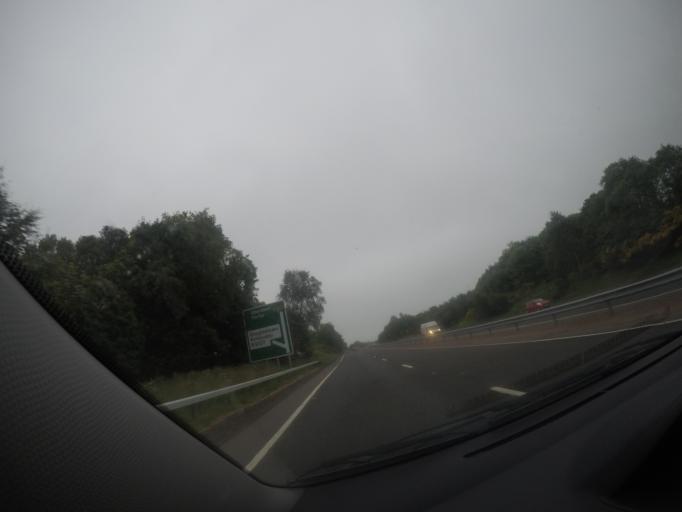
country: GB
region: Scotland
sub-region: Angus
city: Forfar
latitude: 56.5976
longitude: -2.9094
